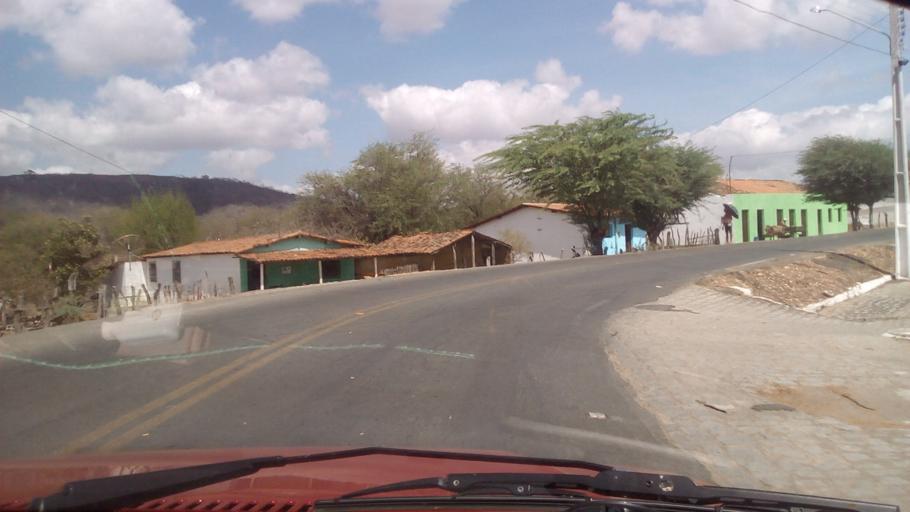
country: BR
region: Paraiba
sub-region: Dona Ines
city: Dona Ines
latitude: -6.5340
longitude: -35.6545
